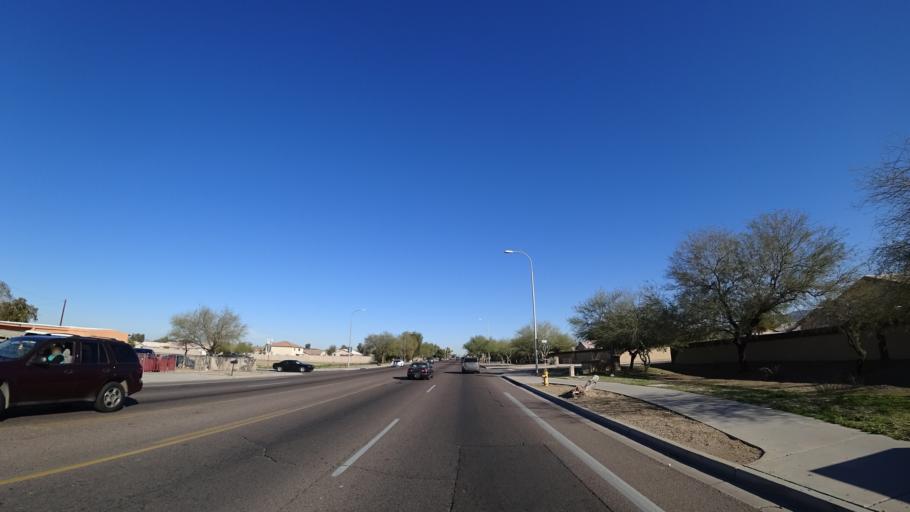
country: US
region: Arizona
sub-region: Maricopa County
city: Phoenix
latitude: 33.3922
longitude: -112.0890
